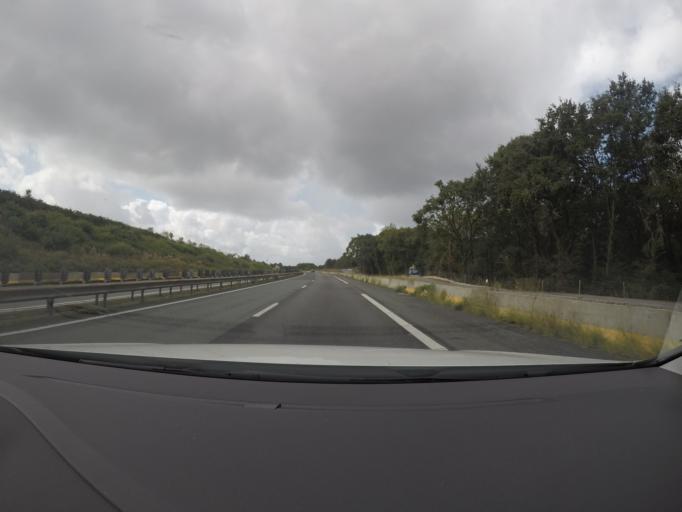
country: FR
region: Aquitaine
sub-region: Departement des Landes
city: Benesse-Maremne
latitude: 43.6488
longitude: -1.3621
